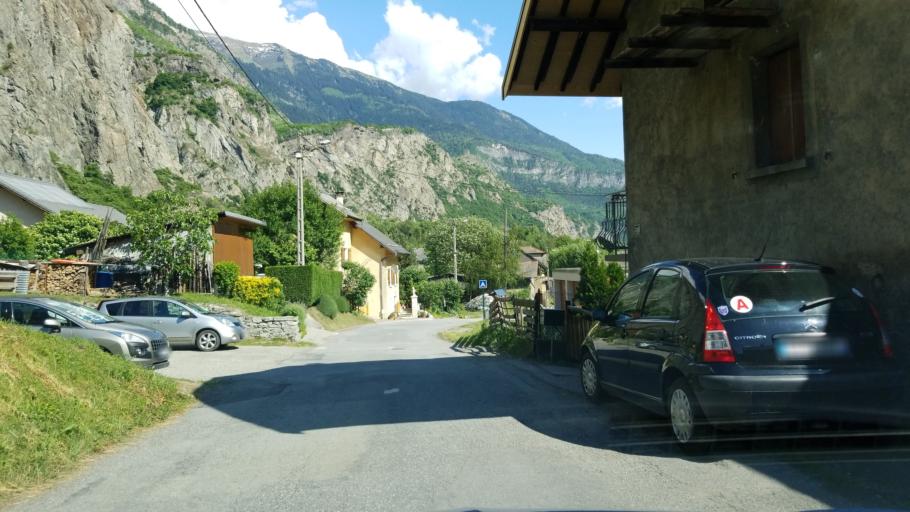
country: FR
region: Rhone-Alpes
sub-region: Departement de la Savoie
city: Saint-Jean-de-Maurienne
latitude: 45.3150
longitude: 6.3380
